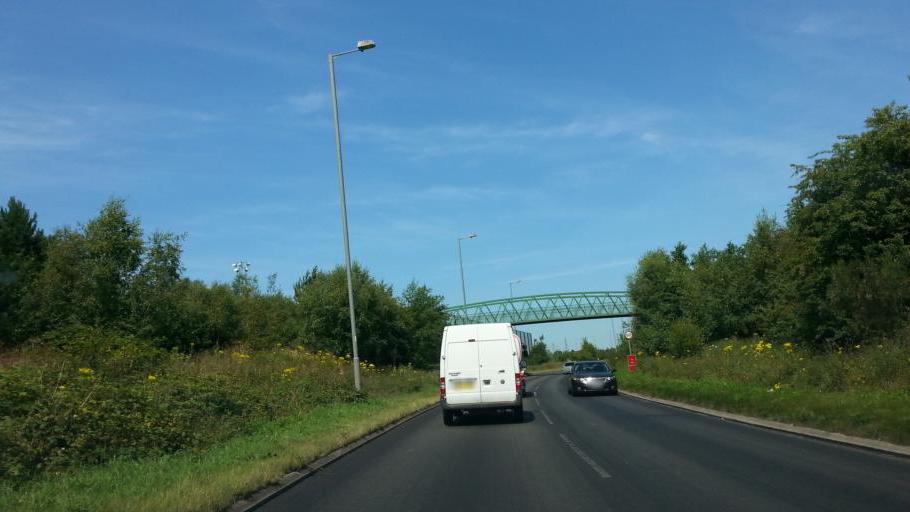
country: GB
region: England
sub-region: Staffordshire
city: Chasetown
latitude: 52.6705
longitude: -1.9422
